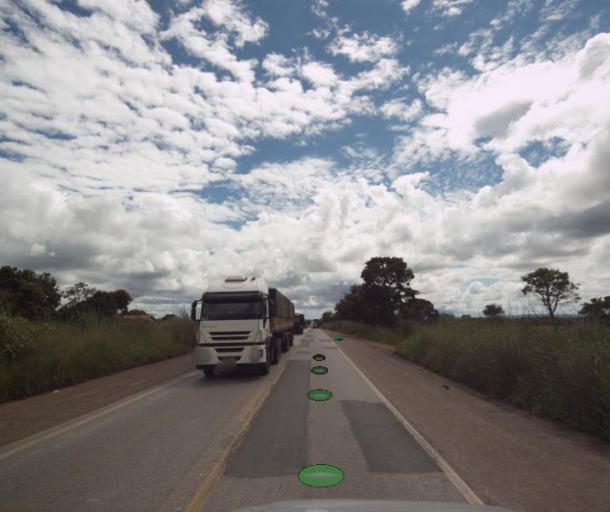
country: BR
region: Goias
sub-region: Uruacu
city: Uruacu
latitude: -14.3264
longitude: -49.1527
